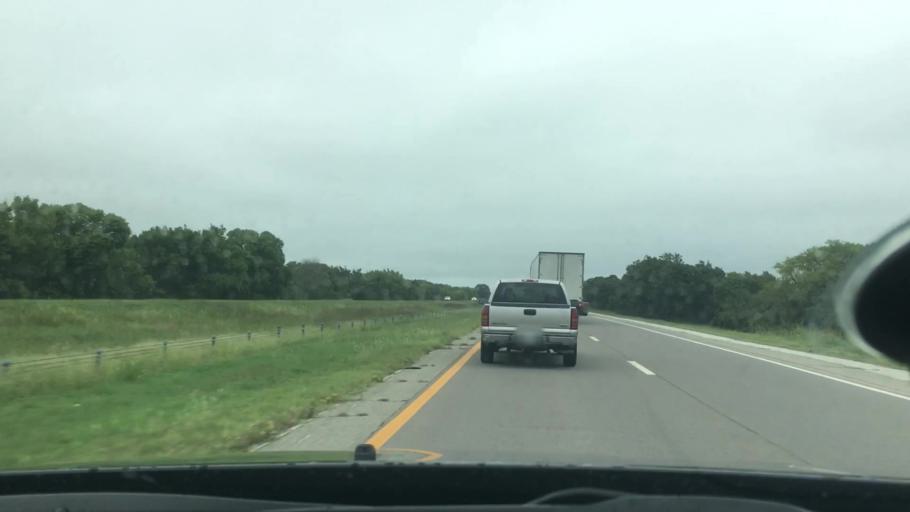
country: US
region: Oklahoma
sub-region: Okfuskee County
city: Okemah
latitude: 35.4283
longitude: -96.2400
